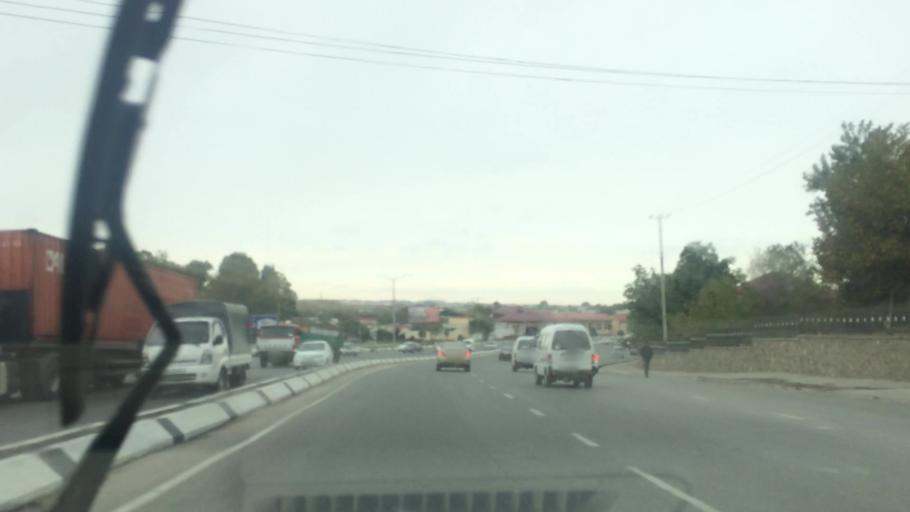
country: UZ
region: Samarqand
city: Samarqand
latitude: 39.6761
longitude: 67.0090
